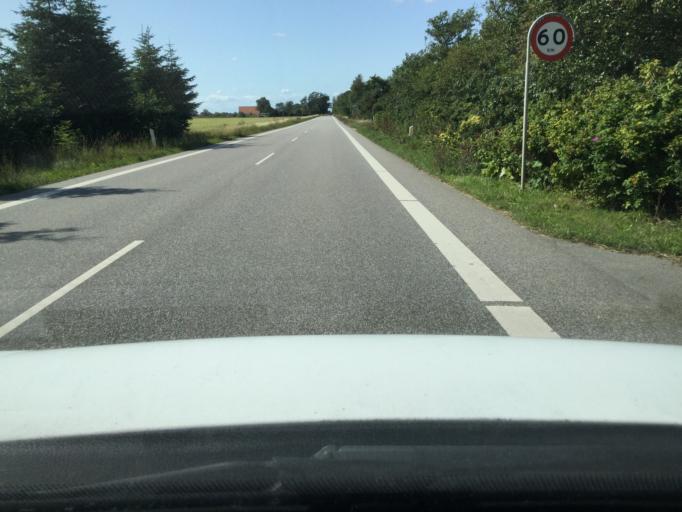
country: DK
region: Zealand
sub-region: Lolland Kommune
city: Rodby
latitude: 54.7586
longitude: 11.3378
